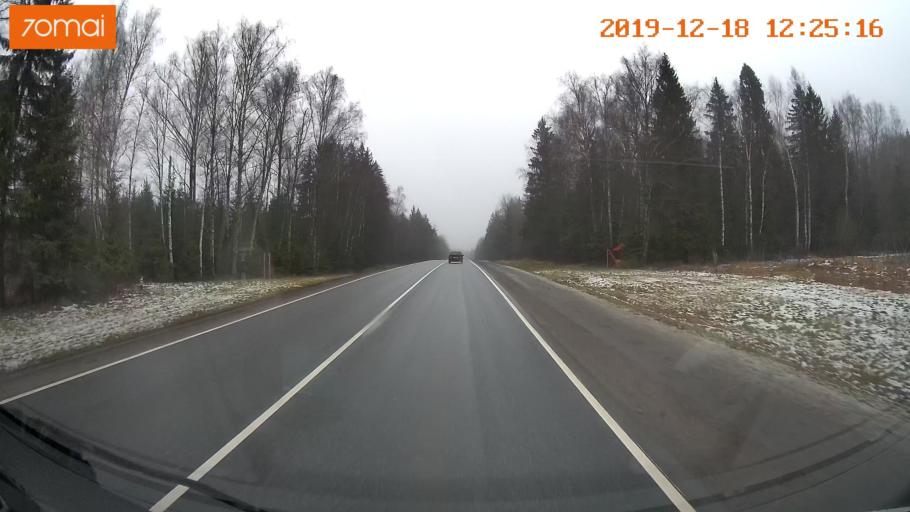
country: RU
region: Moskovskaya
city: Novopetrovskoye
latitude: 56.0355
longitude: 36.4998
